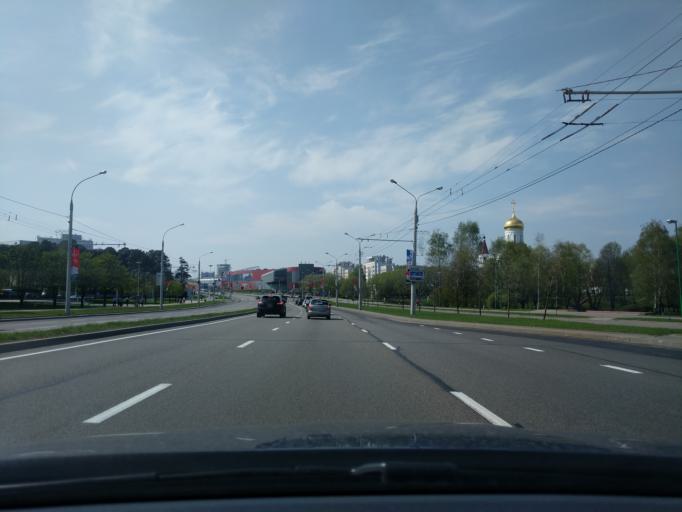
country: BY
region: Minsk
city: Novoye Medvezhino
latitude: 53.9361
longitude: 27.4967
